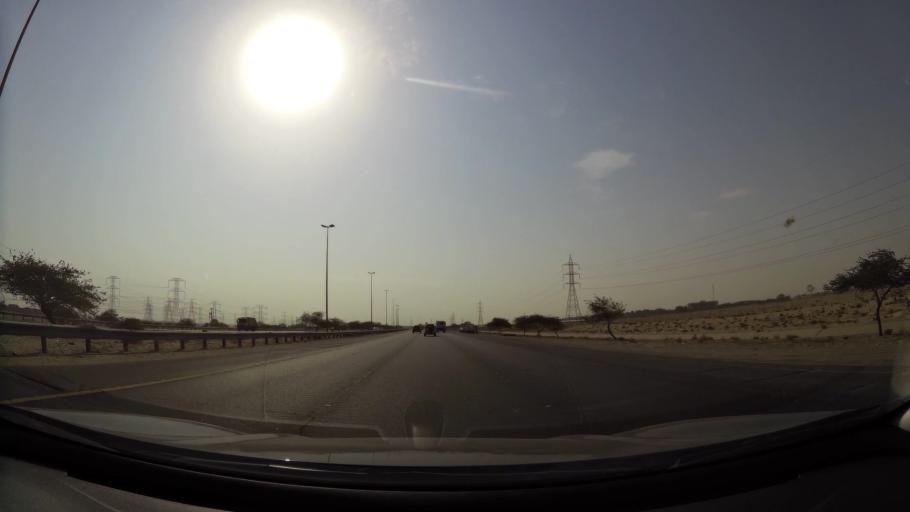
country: KW
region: Al Ahmadi
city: Al Ahmadi
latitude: 28.9691
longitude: 48.1145
